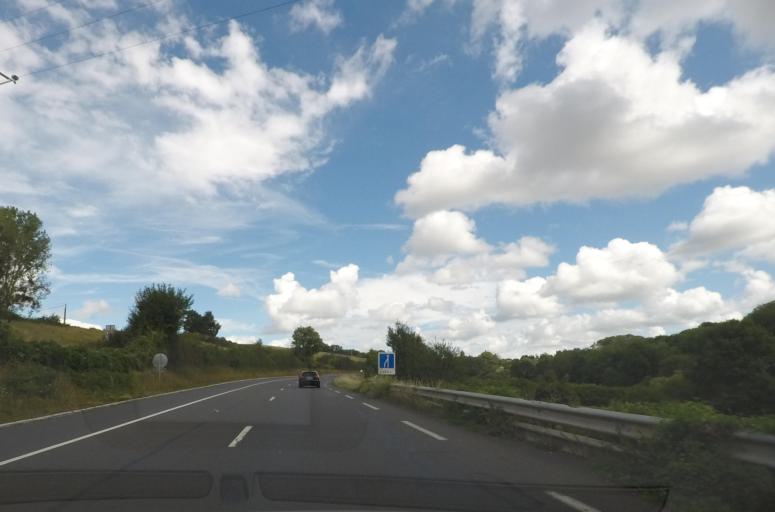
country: FR
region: Pays de la Loire
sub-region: Departement de la Sarthe
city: Clermont-Creans
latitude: 47.7211
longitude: -0.0113
